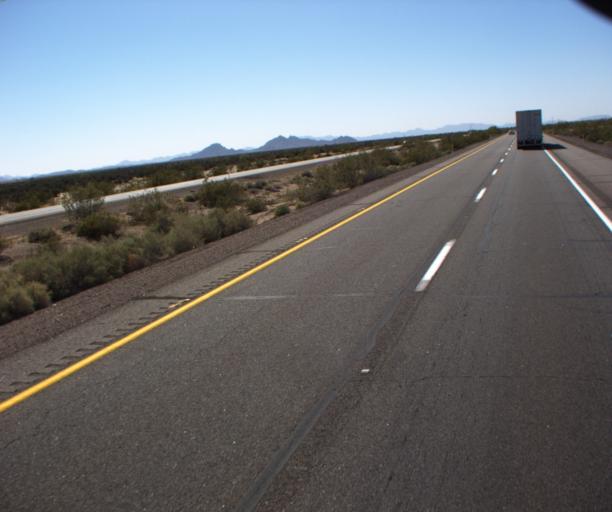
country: US
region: Arizona
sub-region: Yuma County
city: Wellton
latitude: 32.7043
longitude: -113.8835
